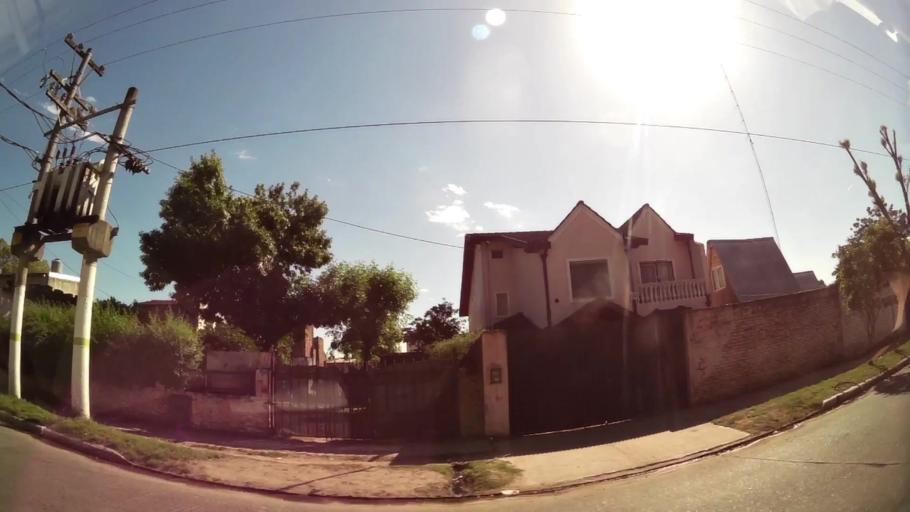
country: AR
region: Buenos Aires
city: Santa Catalina - Dique Lujan
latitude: -34.4856
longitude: -58.6963
